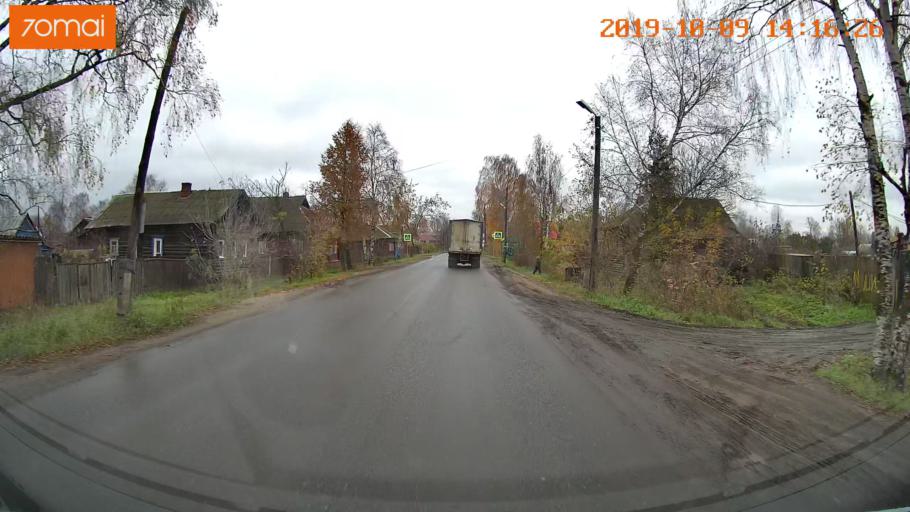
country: RU
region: Kostroma
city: Buy
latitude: 58.4819
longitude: 41.5188
